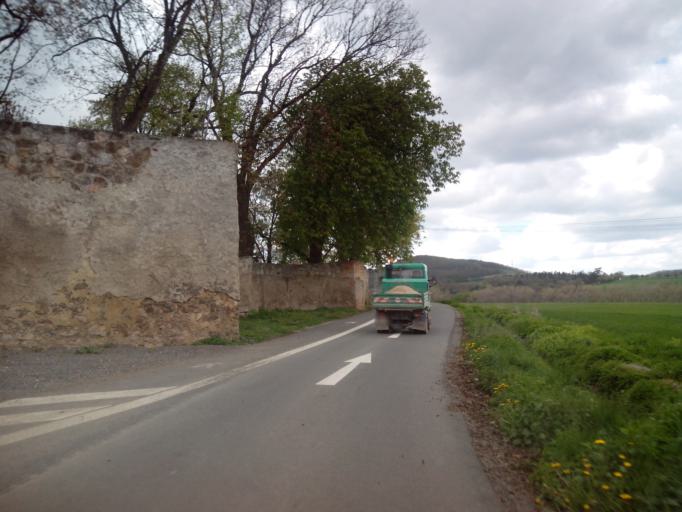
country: CZ
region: Central Bohemia
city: Revnice
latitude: 49.9069
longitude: 14.1503
